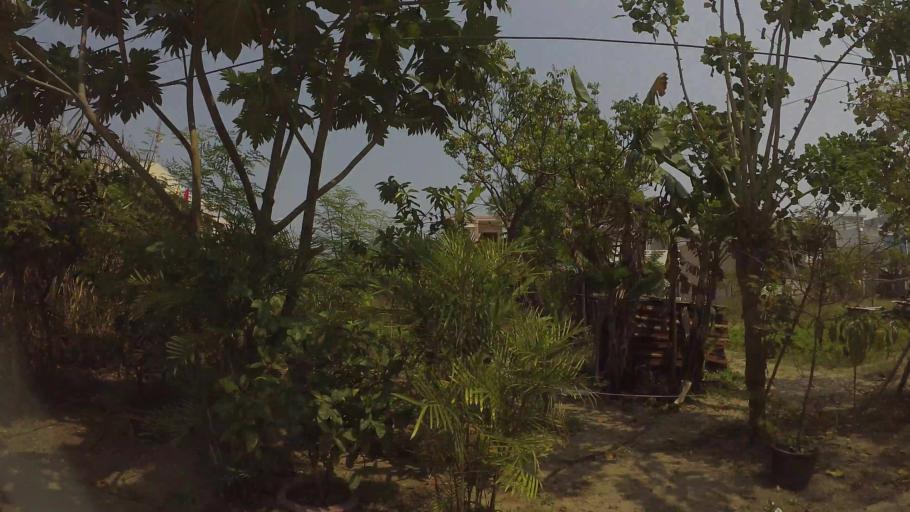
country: VN
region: Da Nang
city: Ngu Hanh Son
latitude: 15.9987
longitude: 108.2652
